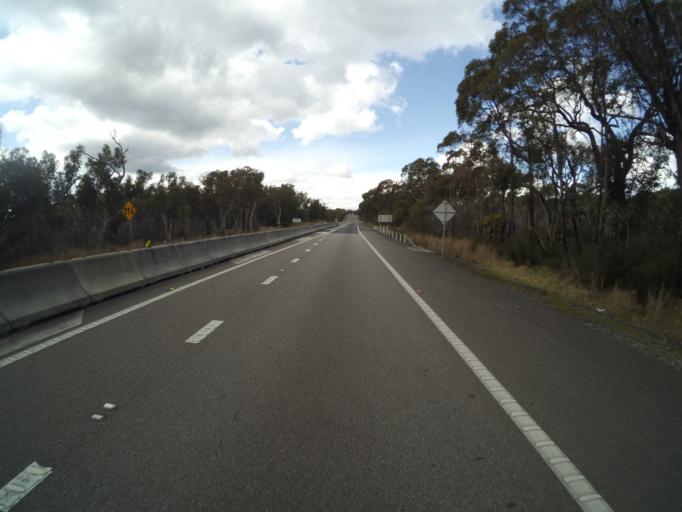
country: AU
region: New South Wales
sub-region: Wollongong
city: Mount Keira
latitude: -34.3260
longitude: 150.7736
